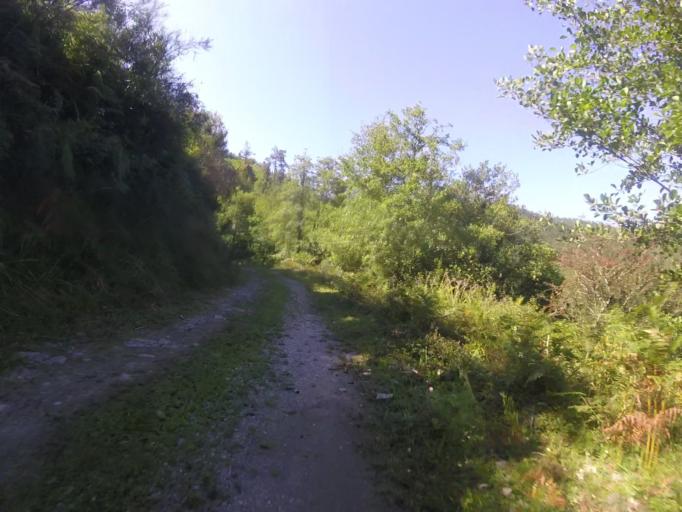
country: ES
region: Navarre
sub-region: Provincia de Navarra
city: Arano
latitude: 43.2208
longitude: -1.8642
